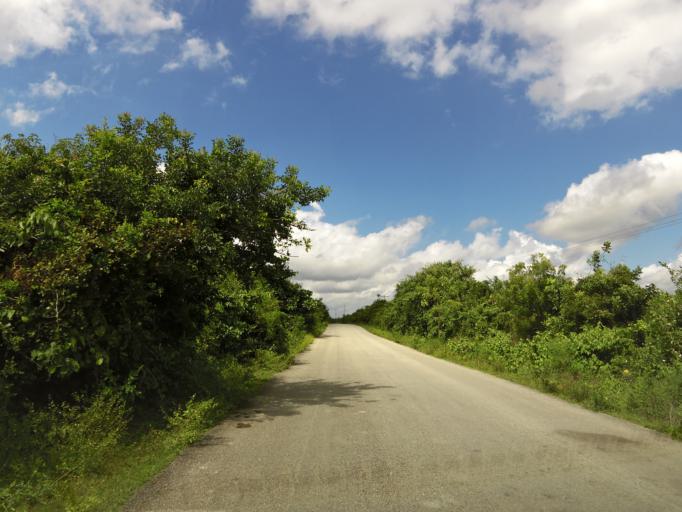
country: TZ
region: Zanzibar Central/South
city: Koani
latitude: -6.1481
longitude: 39.4279
